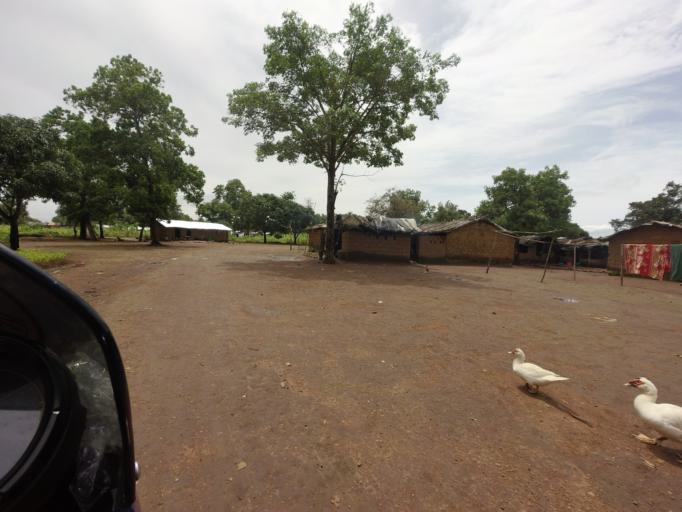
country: SL
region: Northern Province
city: Kambia
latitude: 9.1047
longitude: -12.9192
